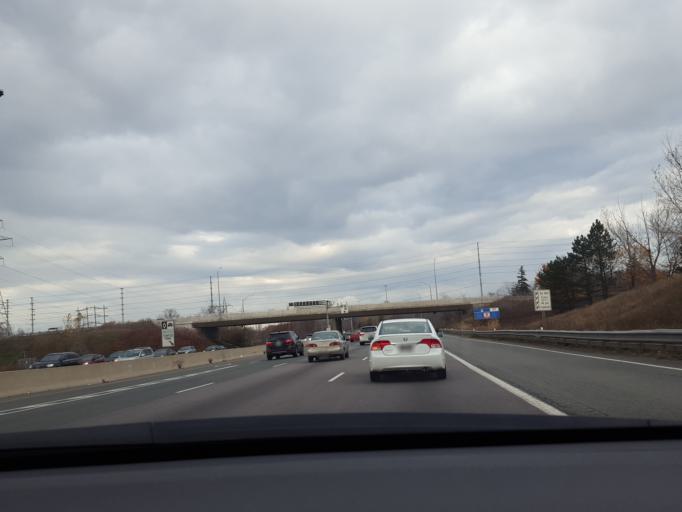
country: CA
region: Ontario
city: Mississauga
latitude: 43.5599
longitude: -79.6870
